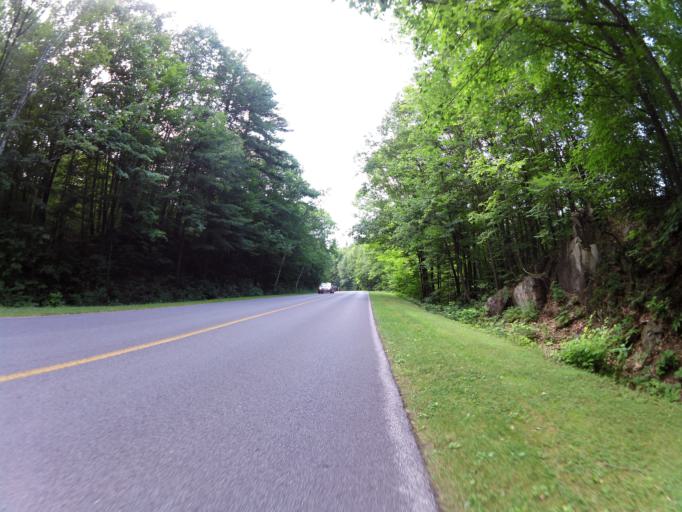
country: CA
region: Quebec
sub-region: Outaouais
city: Gatineau
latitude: 45.4523
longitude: -75.7748
